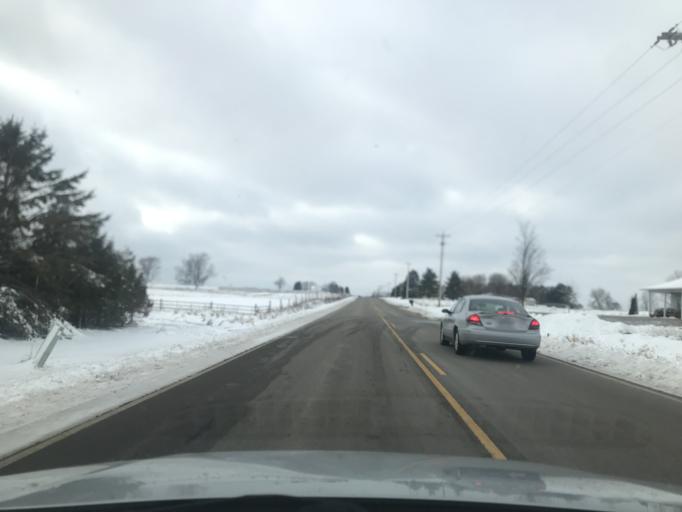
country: US
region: Wisconsin
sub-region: Oconto County
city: Oconto
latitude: 44.9498
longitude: -87.9178
